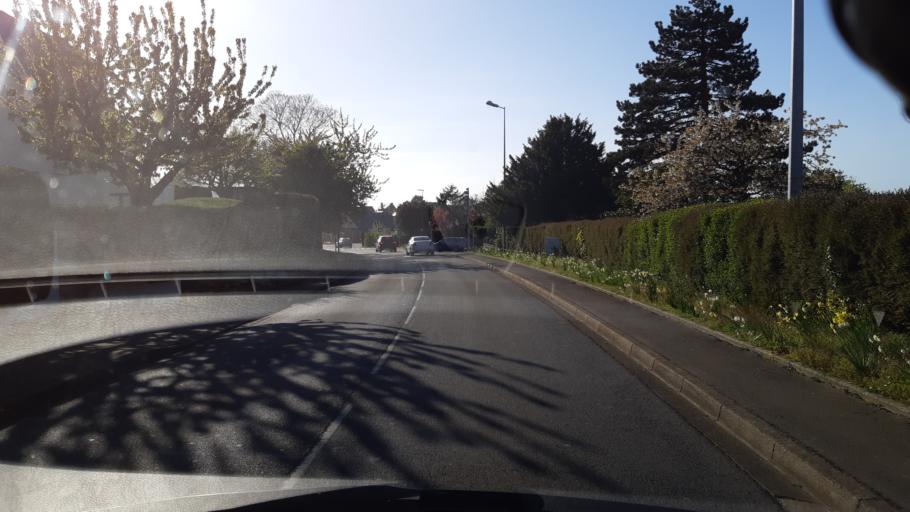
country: FR
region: Lower Normandy
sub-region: Departement de la Manche
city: Saint-Pair-sur-Mer
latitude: 48.8160
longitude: -1.5600
